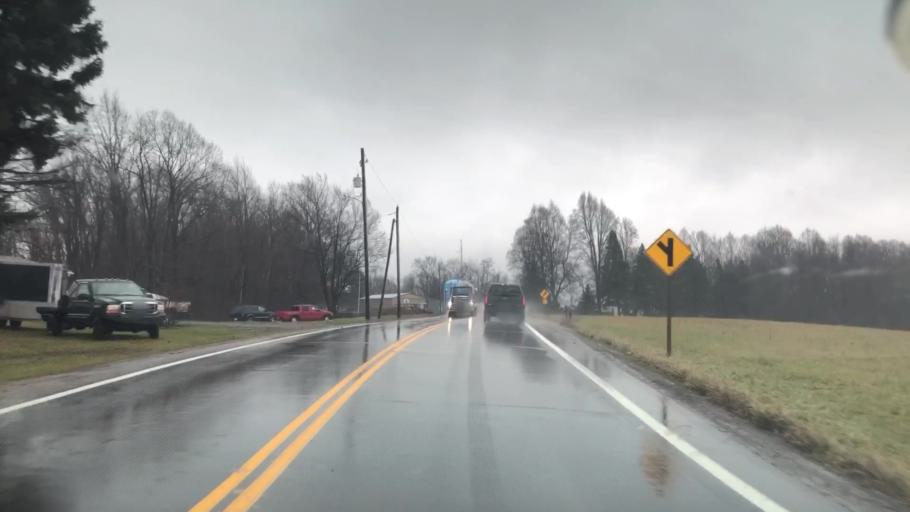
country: US
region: Ohio
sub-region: Harrison County
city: Cadiz
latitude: 40.1951
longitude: -80.9970
